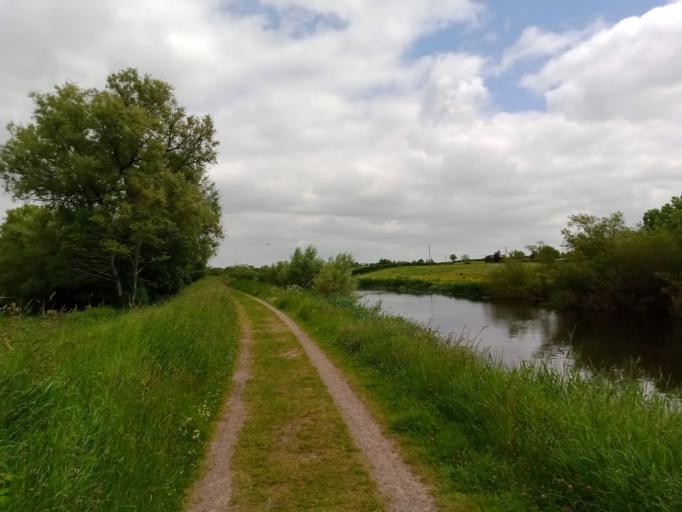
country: IE
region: Leinster
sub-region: County Carlow
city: Bagenalstown
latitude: 52.7469
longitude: -6.9695
